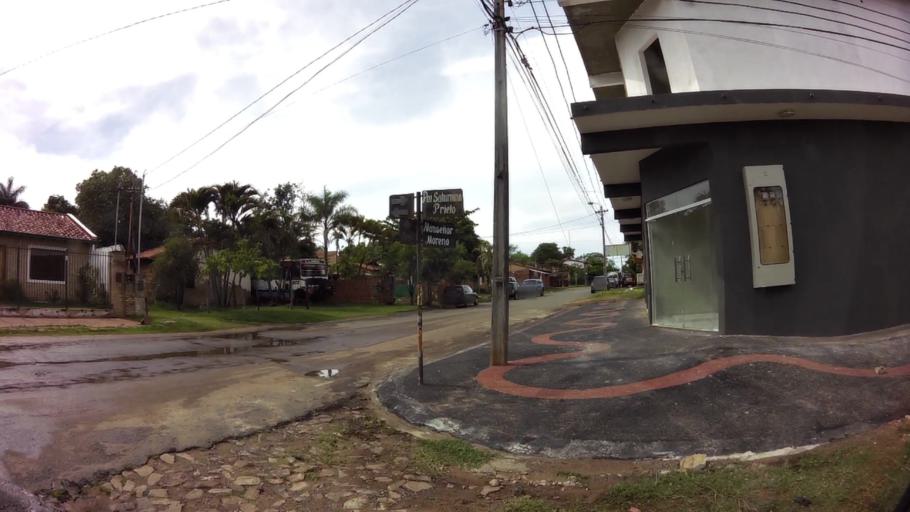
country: PY
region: Central
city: Limpio
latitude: -25.1649
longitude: -57.4788
